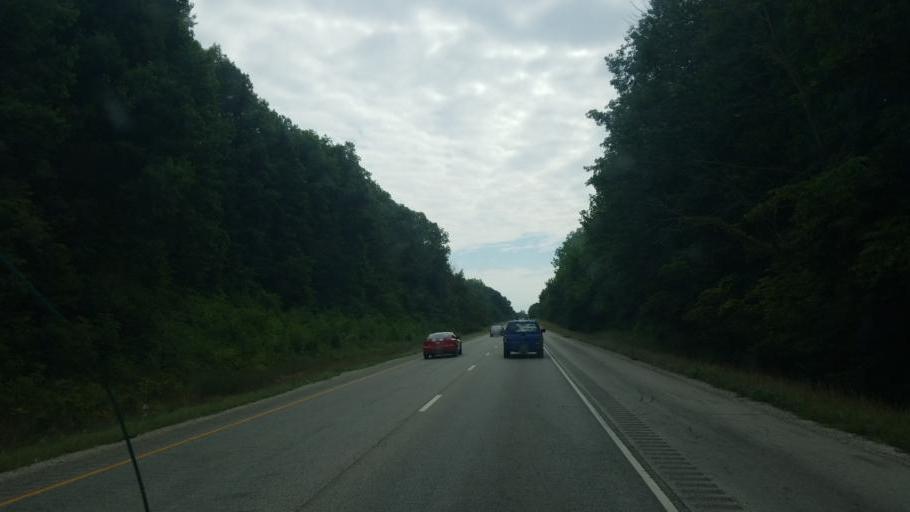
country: US
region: Indiana
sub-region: Vigo County
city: Seelyville
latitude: 39.4434
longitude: -87.2661
